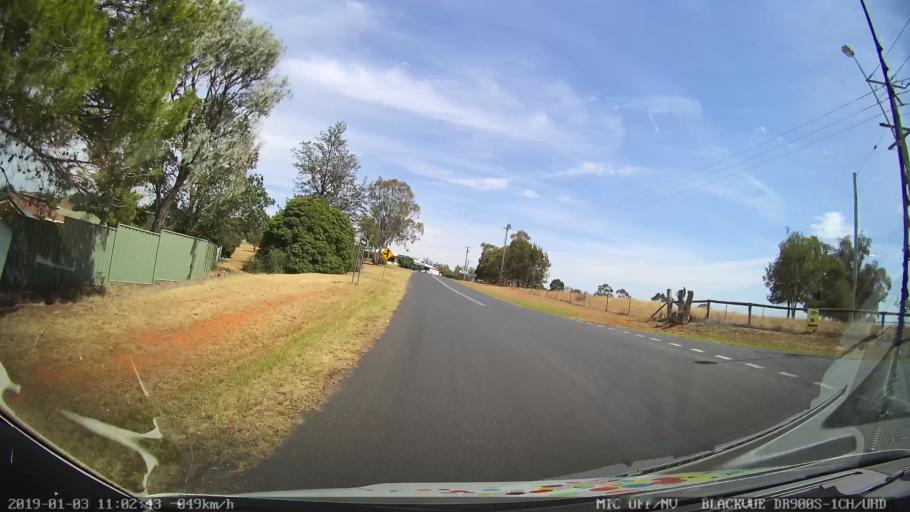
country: AU
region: New South Wales
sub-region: Young
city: Young
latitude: -34.2960
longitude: 148.2981
